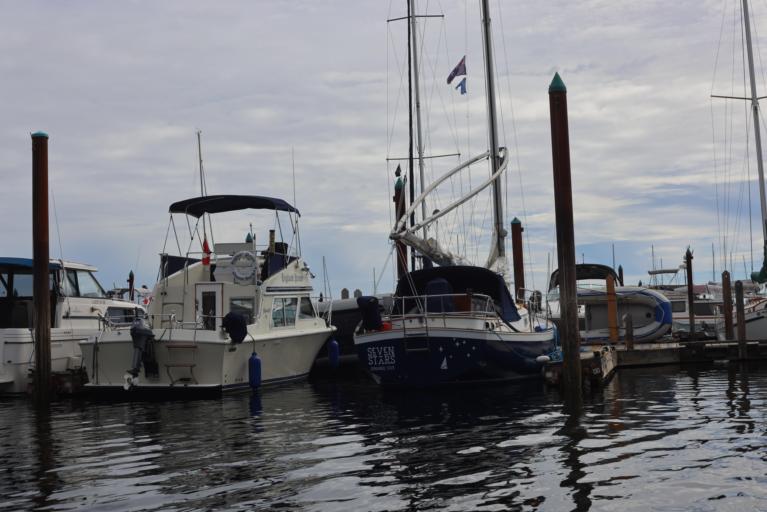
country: CA
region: British Columbia
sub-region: Regional District of Nanaimo
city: Parksville
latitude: 49.2866
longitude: -124.1373
